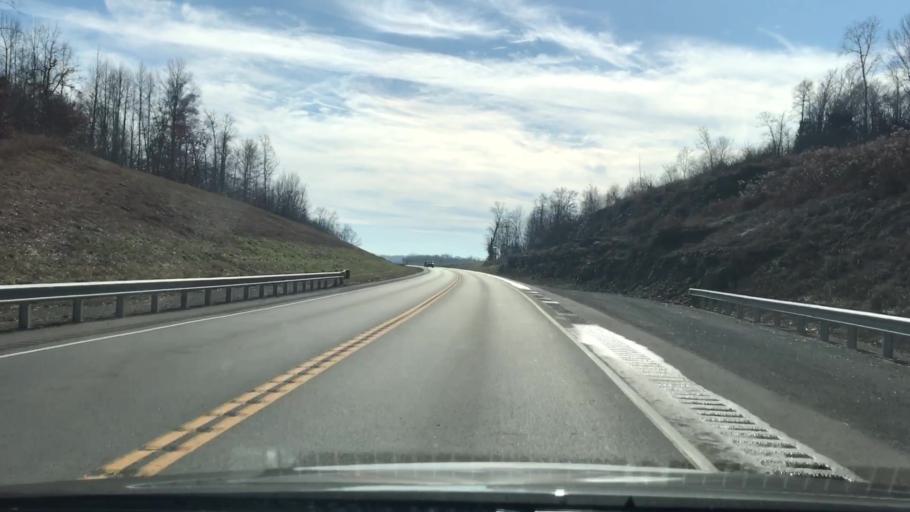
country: US
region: Kentucky
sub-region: Monroe County
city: Tompkinsville
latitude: 36.8227
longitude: -85.6885
